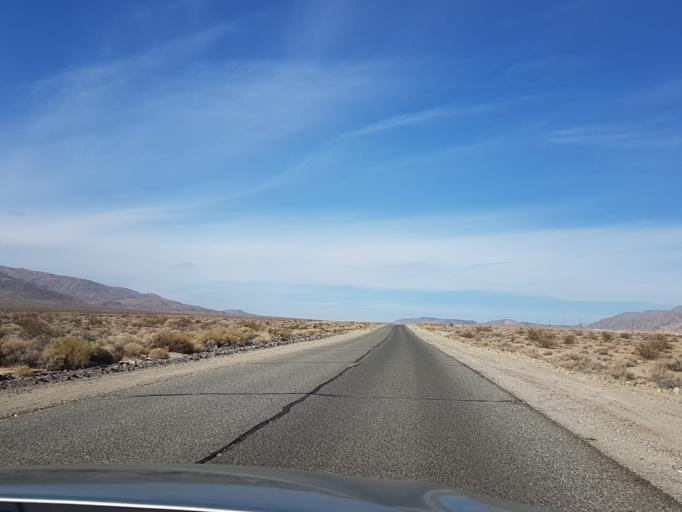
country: US
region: California
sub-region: San Bernardino County
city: Searles Valley
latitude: 35.8343
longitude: -117.3373
